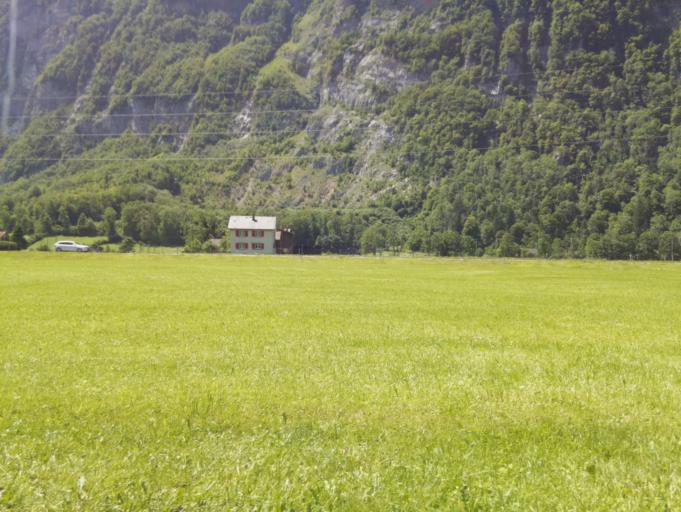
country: CH
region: Glarus
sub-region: Glarus
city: Netstal
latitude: 47.0764
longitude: 9.0569
